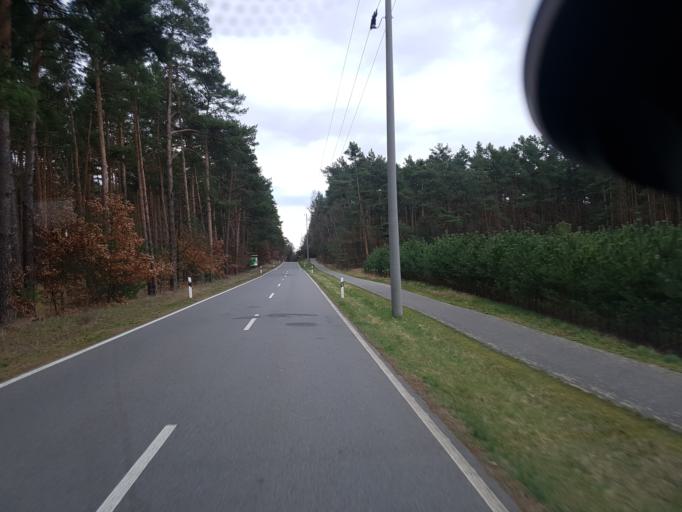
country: DE
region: Brandenburg
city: Mixdorf
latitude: 52.1887
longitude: 14.4265
